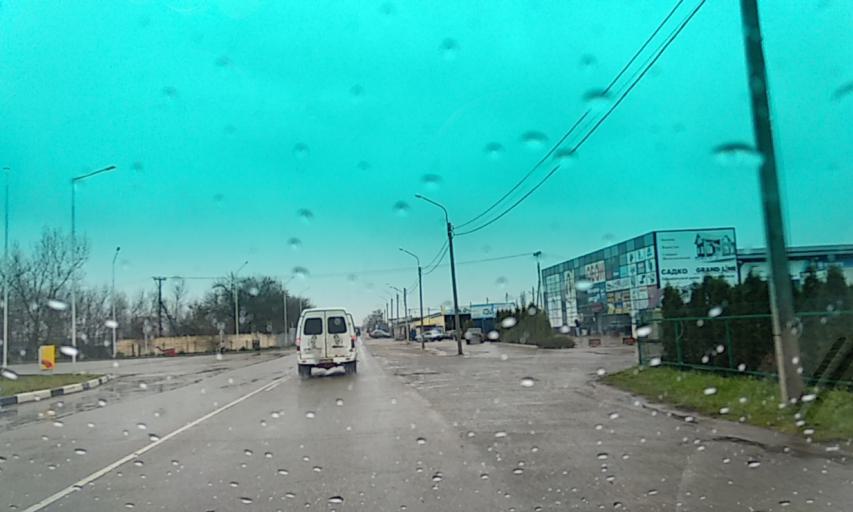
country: RU
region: Krasnodarskiy
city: Belorechensk
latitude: 44.7943
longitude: 39.8623
